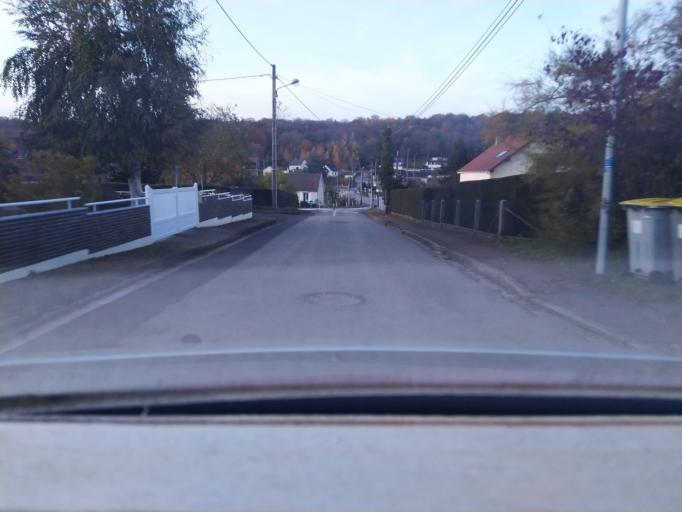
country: FR
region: Haute-Normandie
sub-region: Departement de la Seine-Maritime
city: Yainville
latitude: 49.4579
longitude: 0.8341
